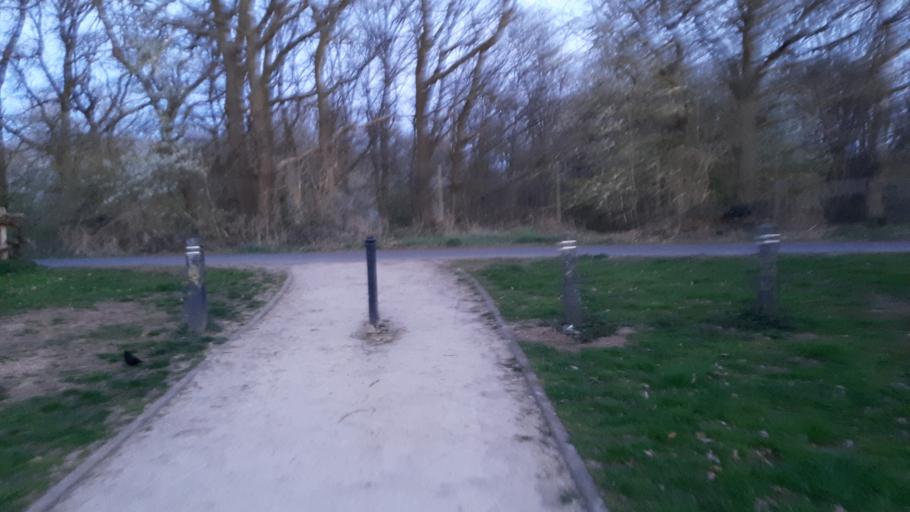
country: DE
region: North Rhine-Westphalia
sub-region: Regierungsbezirk Koln
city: Mechernich
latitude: 50.5952
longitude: 6.6622
